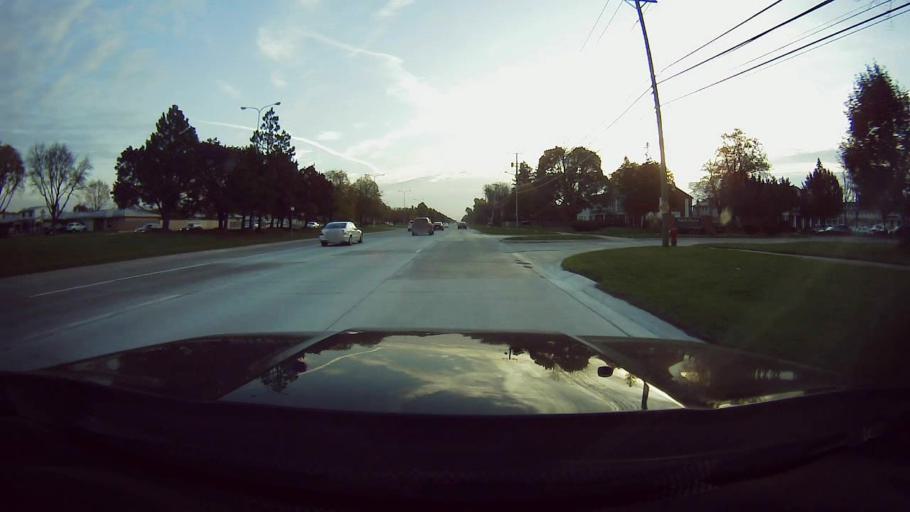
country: US
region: Michigan
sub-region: Macomb County
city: Sterling Heights
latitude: 42.5641
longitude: -83.0790
